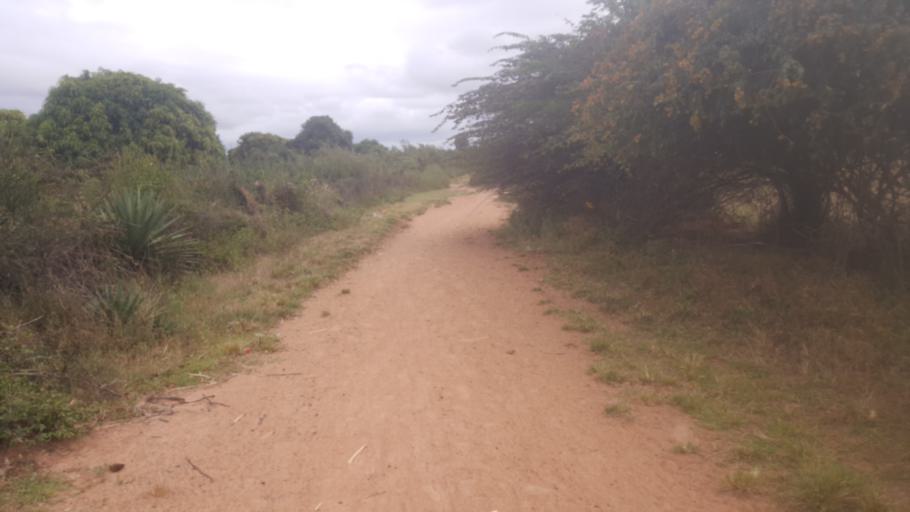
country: TZ
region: Dodoma
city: Msanga
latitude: -6.0392
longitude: 35.9381
